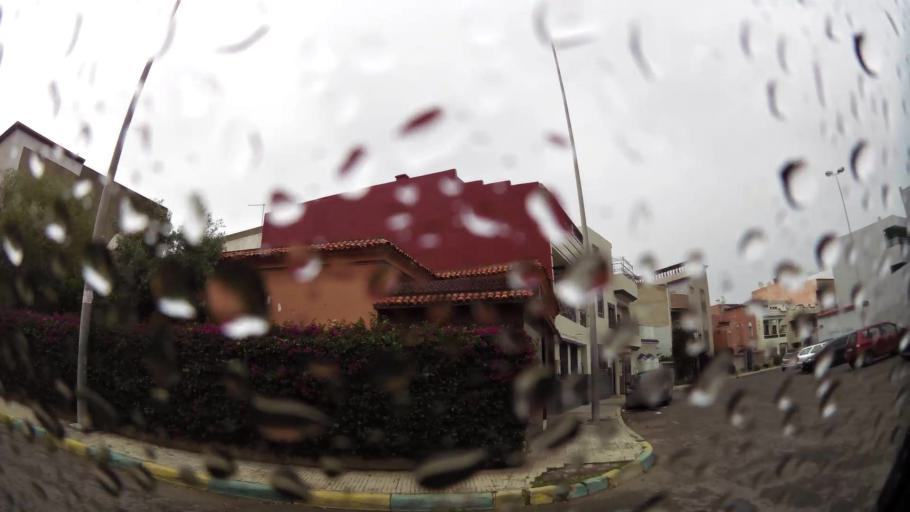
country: MA
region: Grand Casablanca
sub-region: Mediouna
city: Tit Mellil
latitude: 33.6158
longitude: -7.4878
